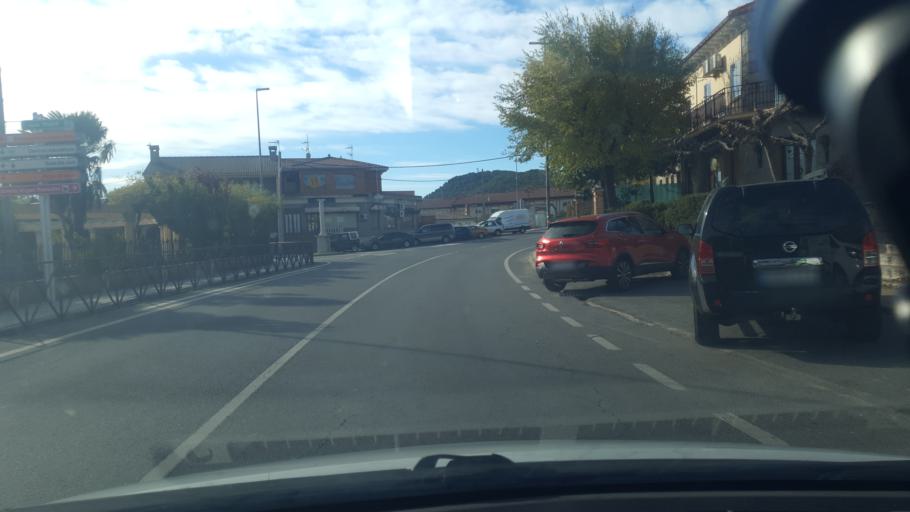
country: ES
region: Castille and Leon
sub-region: Provincia de Avila
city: Sotillo de la Adrada
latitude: 40.2936
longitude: -4.5871
